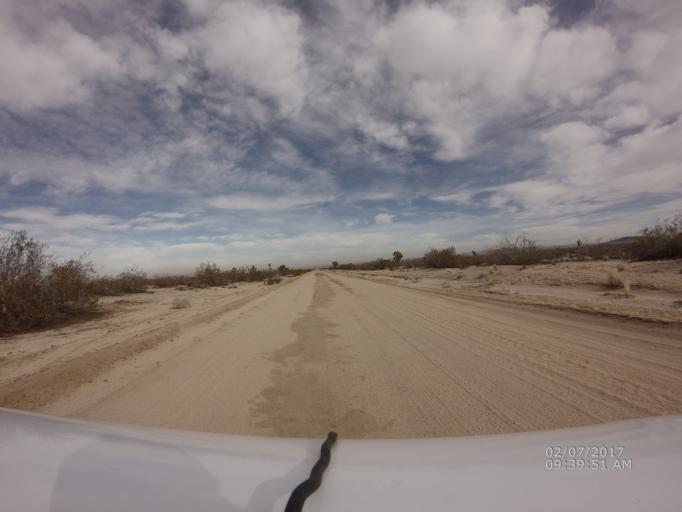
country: US
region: California
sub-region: Los Angeles County
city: Lake Los Angeles
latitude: 34.5552
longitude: -117.7114
